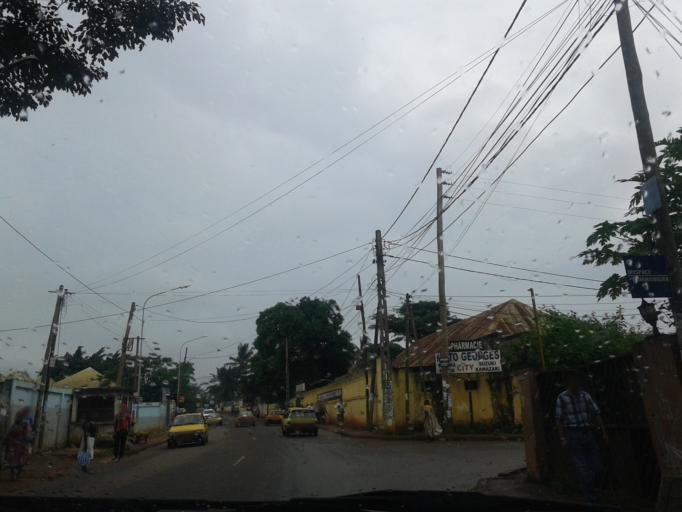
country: CM
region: Centre
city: Yaounde
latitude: 3.8882
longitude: 11.5157
